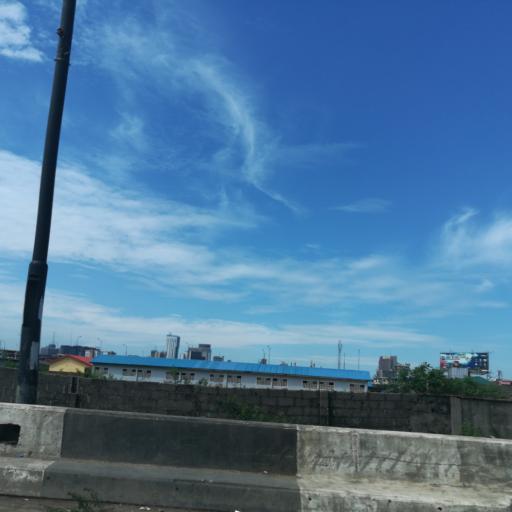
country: NG
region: Lagos
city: Lagos
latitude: 6.4647
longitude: 3.3950
